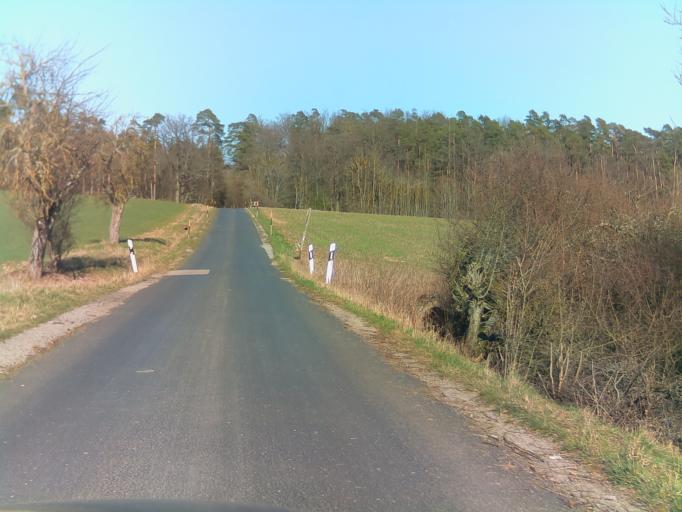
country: DE
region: Bavaria
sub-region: Regierungsbezirk Unterfranken
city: Willmars
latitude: 50.4928
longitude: 10.2878
